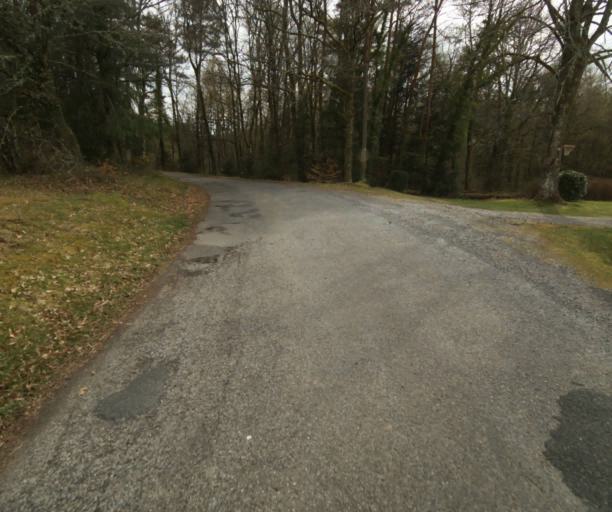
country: FR
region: Limousin
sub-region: Departement de la Correze
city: Argentat
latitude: 45.2099
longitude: 1.9578
